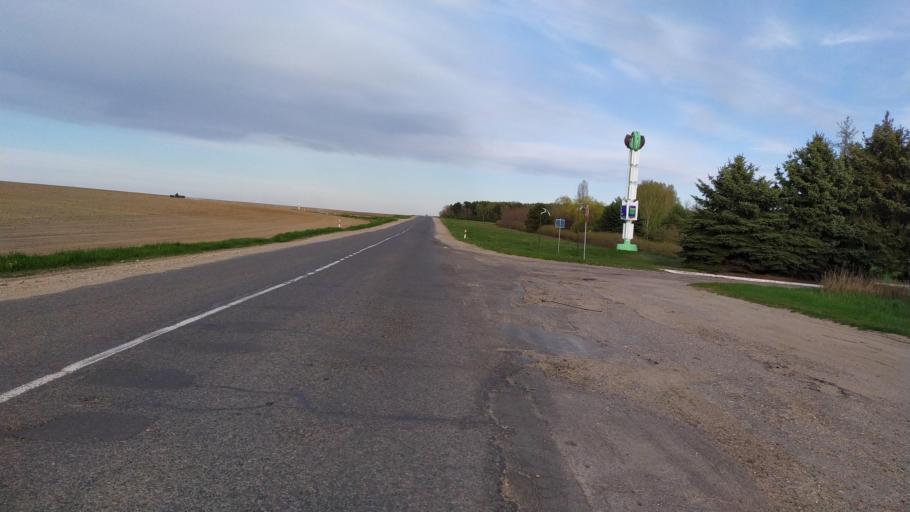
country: BY
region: Brest
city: Kamyanyets
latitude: 52.4176
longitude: 23.6871
